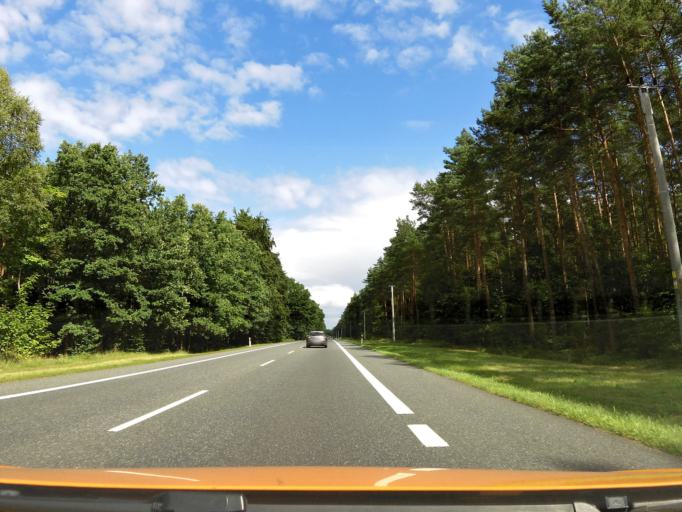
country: PL
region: West Pomeranian Voivodeship
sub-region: Powiat goleniowski
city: Osina
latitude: 53.6185
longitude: 14.9502
